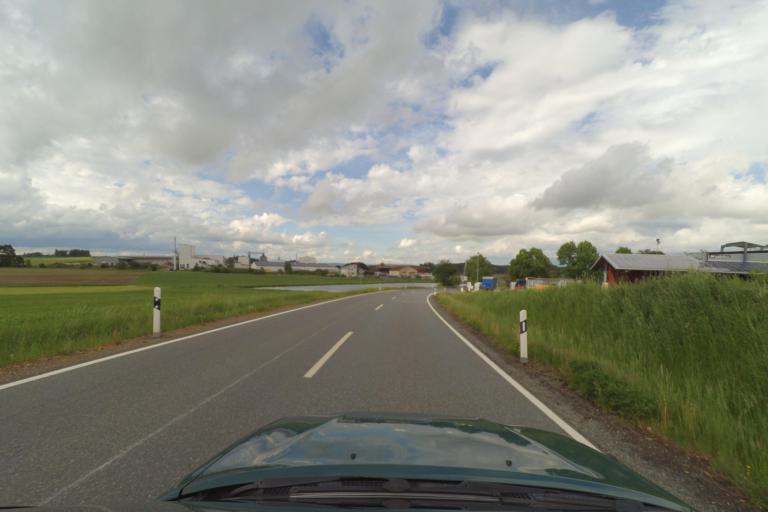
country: DE
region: Bavaria
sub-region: Upper Palatinate
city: Tirschenreuth
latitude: 49.8249
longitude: 12.3197
